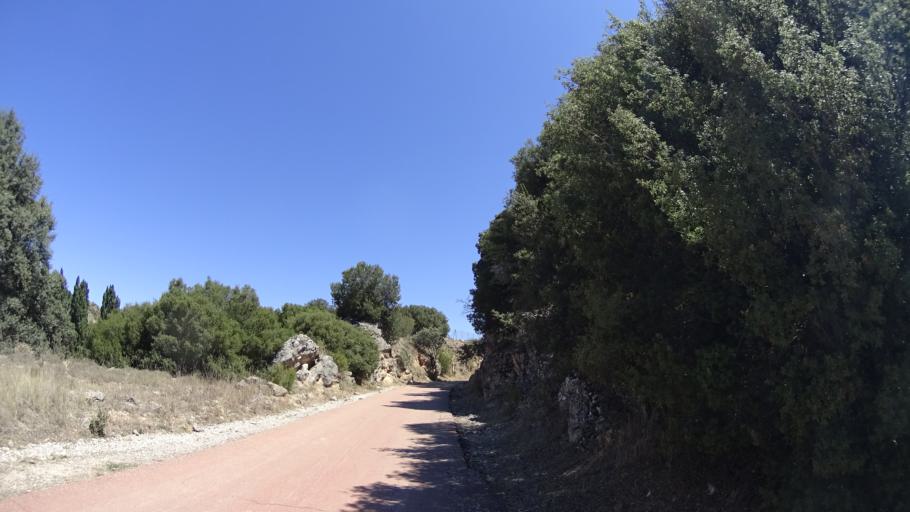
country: ES
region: Madrid
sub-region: Provincia de Madrid
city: Ambite
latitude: 40.2936
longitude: -3.1973
